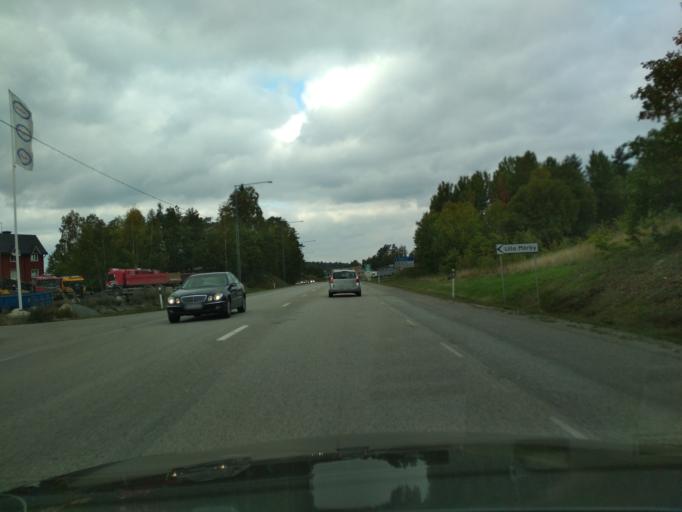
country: SE
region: Stockholm
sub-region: Vallentuna Kommun
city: Vallentuna
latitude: 59.5396
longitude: 18.0529
